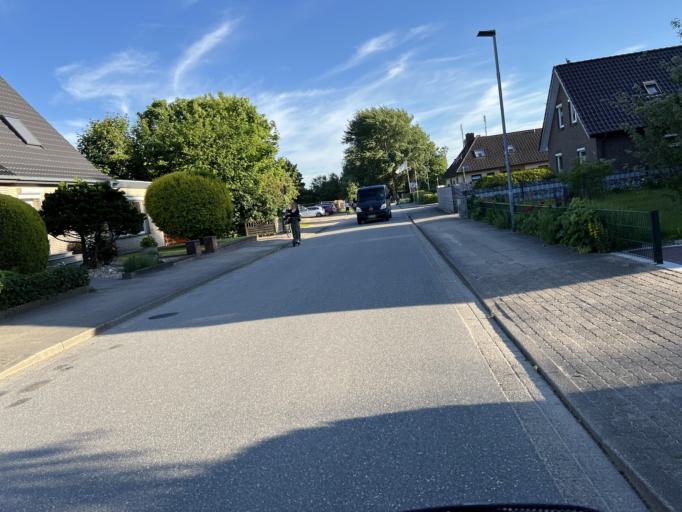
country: DE
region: Schleswig-Holstein
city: Wesseln
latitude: 54.1896
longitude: 9.0830
